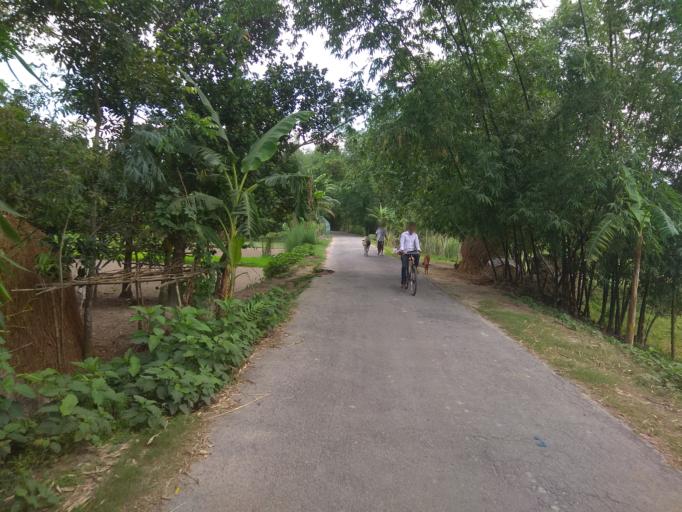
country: IN
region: West Bengal
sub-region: Koch Bihar
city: Haldibari
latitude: 26.2005
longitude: 88.9215
